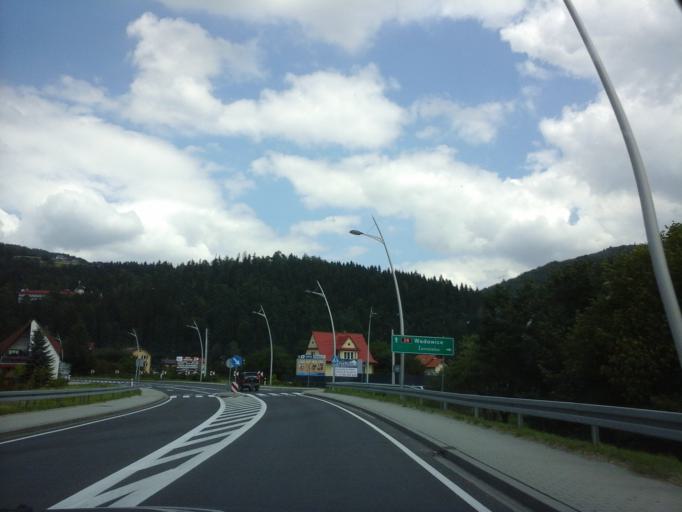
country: PL
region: Lesser Poland Voivodeship
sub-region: Powiat suski
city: Makow Podhalanski
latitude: 49.7229
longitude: 19.6905
